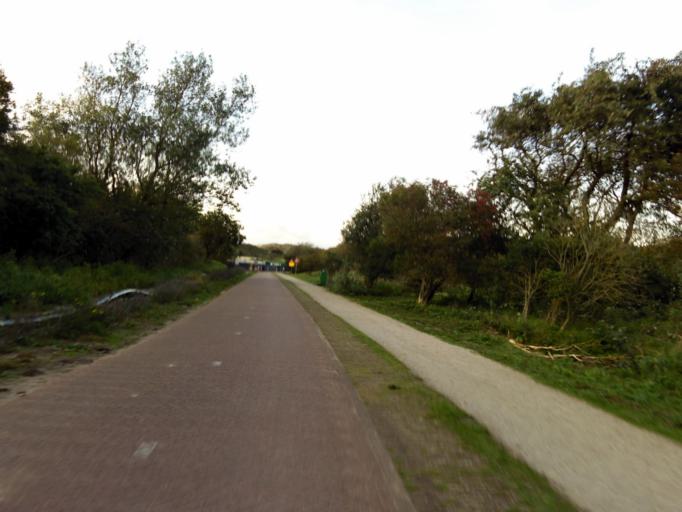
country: NL
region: South Holland
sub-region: Gemeente Den Haag
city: Scheveningen
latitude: 52.1229
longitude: 4.3054
